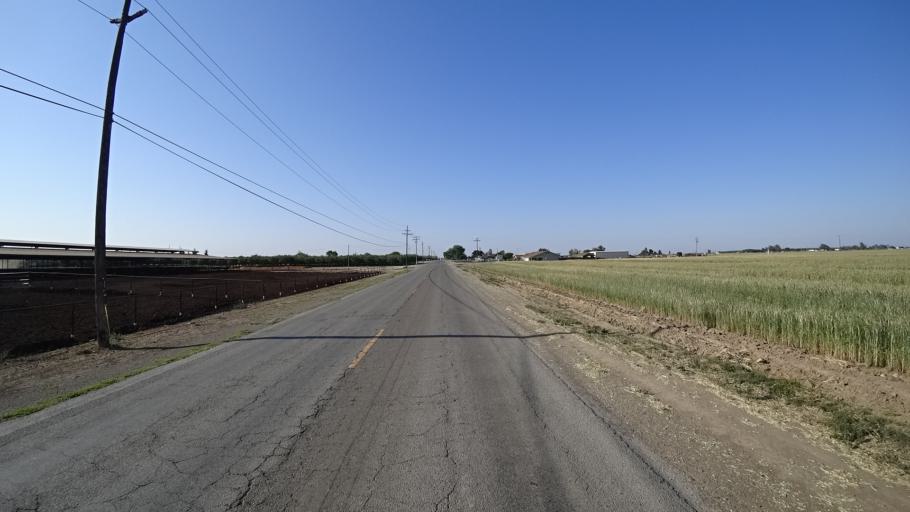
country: US
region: California
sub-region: Kings County
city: Home Garden
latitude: 36.3222
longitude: -119.5653
